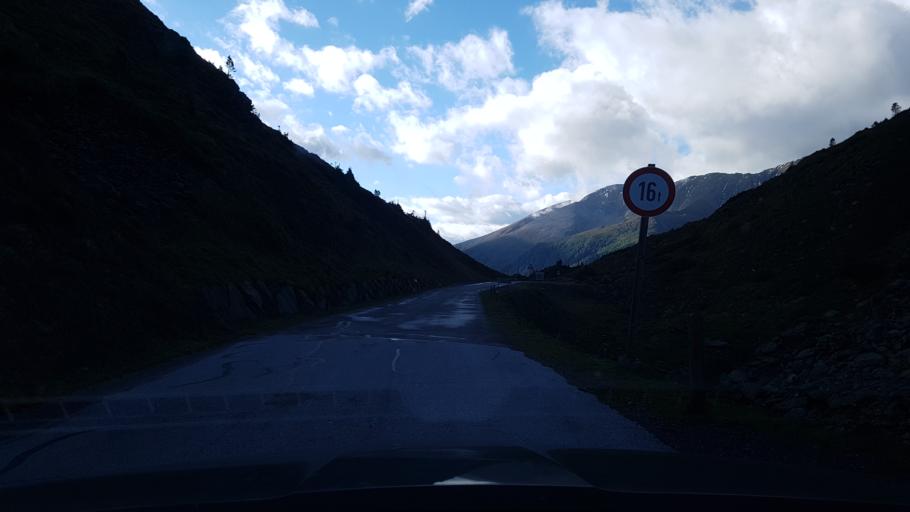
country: AT
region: Styria
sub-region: Politischer Bezirk Liezen
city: Sankt Nikolai im Solktal
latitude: 47.2714
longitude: 14.0797
